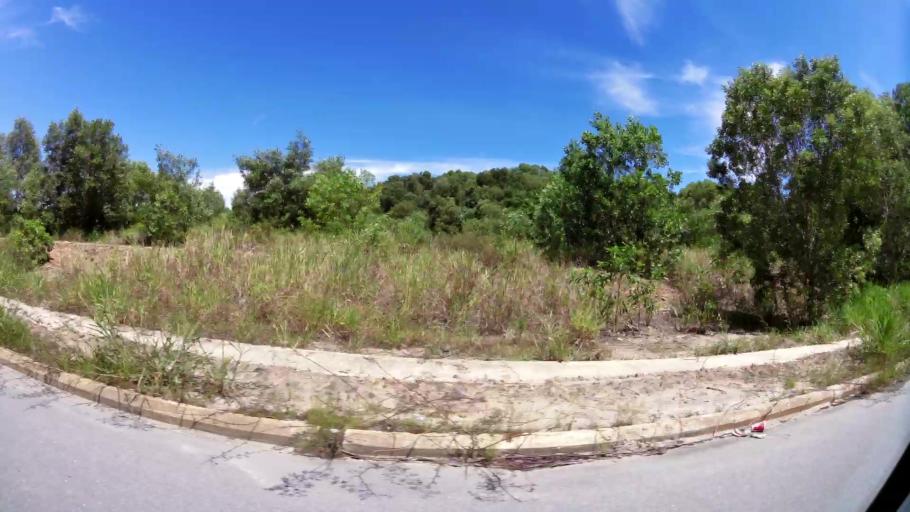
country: BN
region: Brunei and Muara
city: Bandar Seri Begawan
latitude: 5.0339
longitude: 115.0353
